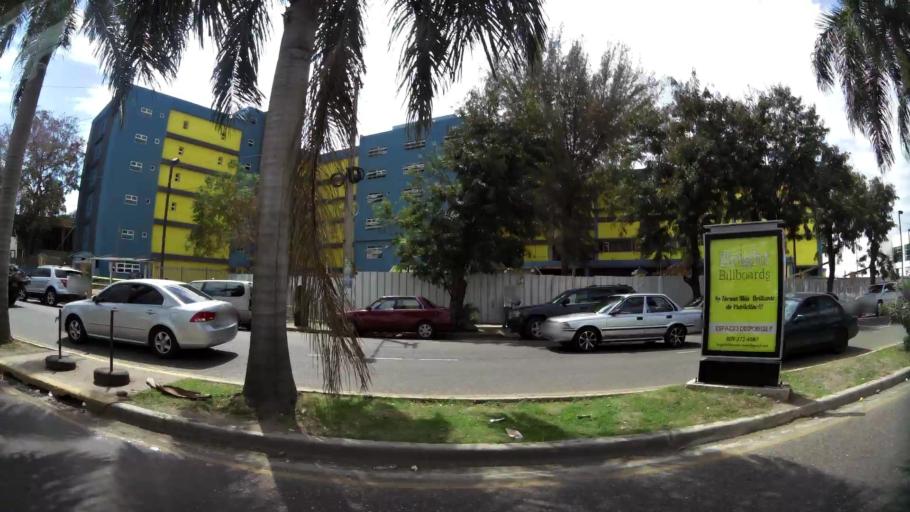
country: DO
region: Santiago
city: Santiago de los Caballeros
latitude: 19.4571
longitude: -70.6996
